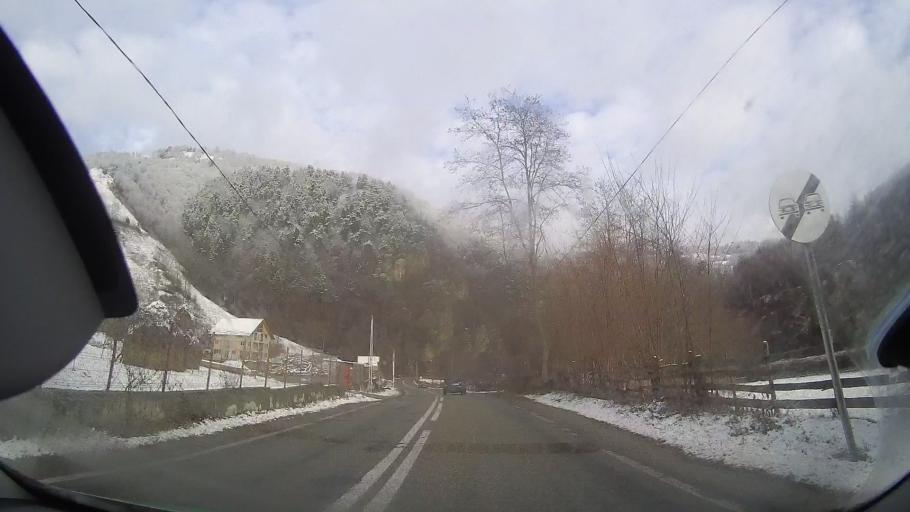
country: RO
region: Alba
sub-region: Oras Baia de Aries
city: Baia de Aries
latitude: 46.3987
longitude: 23.3009
